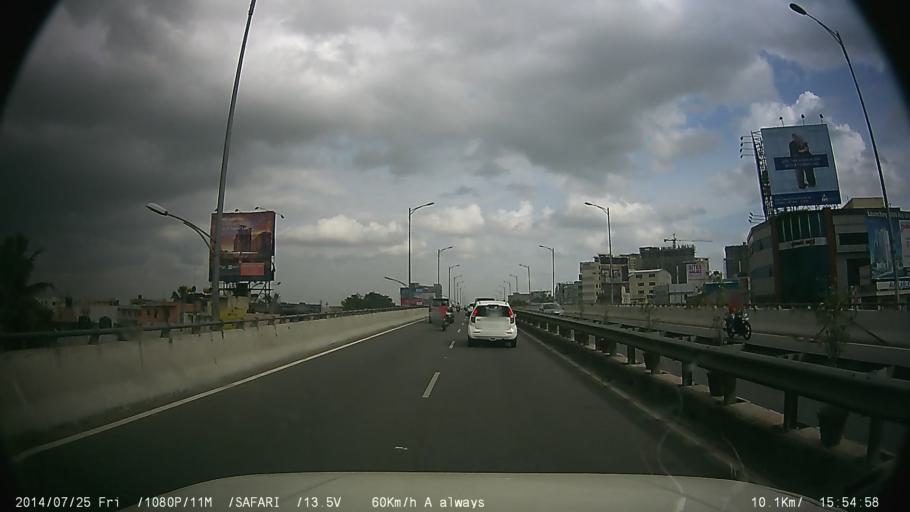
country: IN
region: Karnataka
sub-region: Bangalore Urban
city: Bangalore
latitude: 12.9072
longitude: 77.6288
